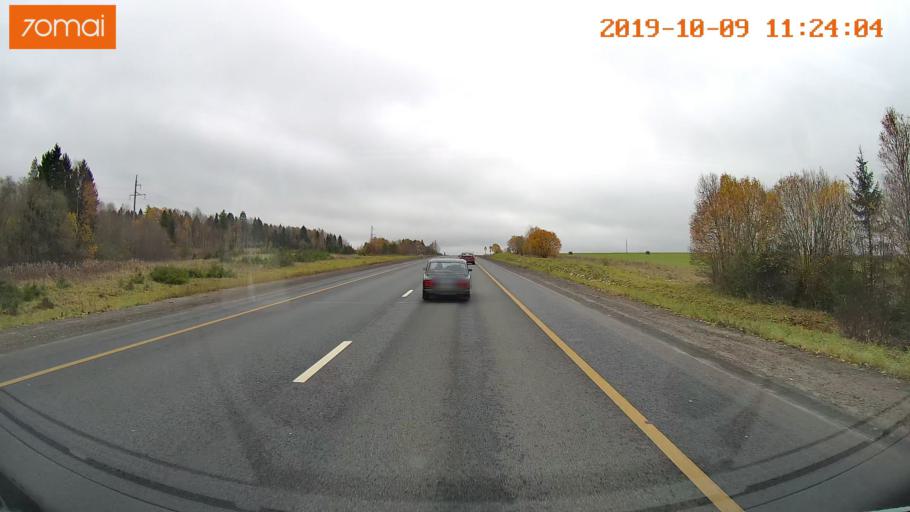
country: RU
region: Vologda
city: Vologda
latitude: 59.1148
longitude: 39.9763
